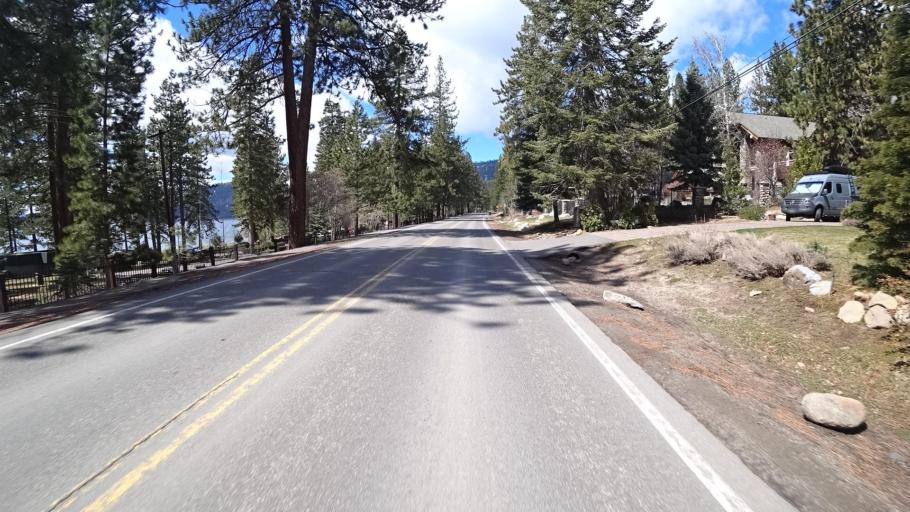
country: US
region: Nevada
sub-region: Washoe County
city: Incline Village
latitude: 39.2461
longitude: -119.9670
